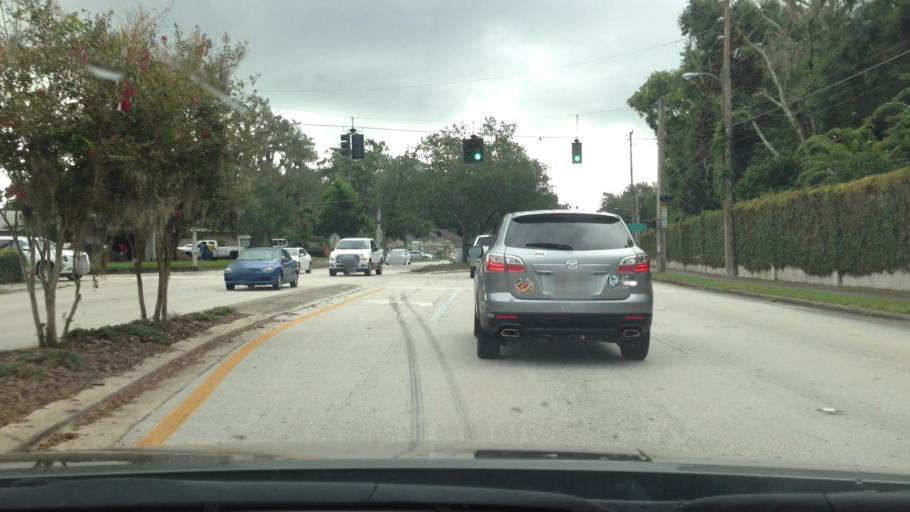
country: US
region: Florida
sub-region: Orange County
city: Maitland
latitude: 28.6281
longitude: -81.3469
